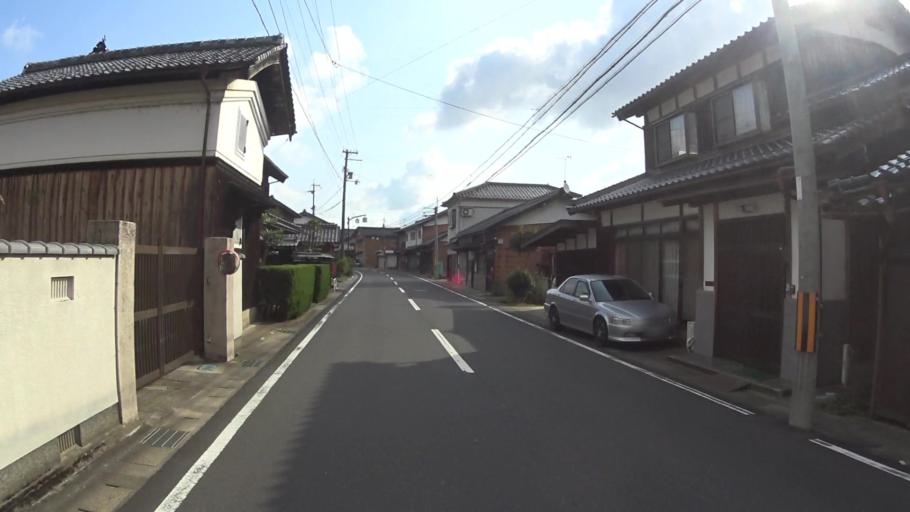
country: JP
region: Kyoto
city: Miyazu
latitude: 35.5618
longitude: 135.1455
